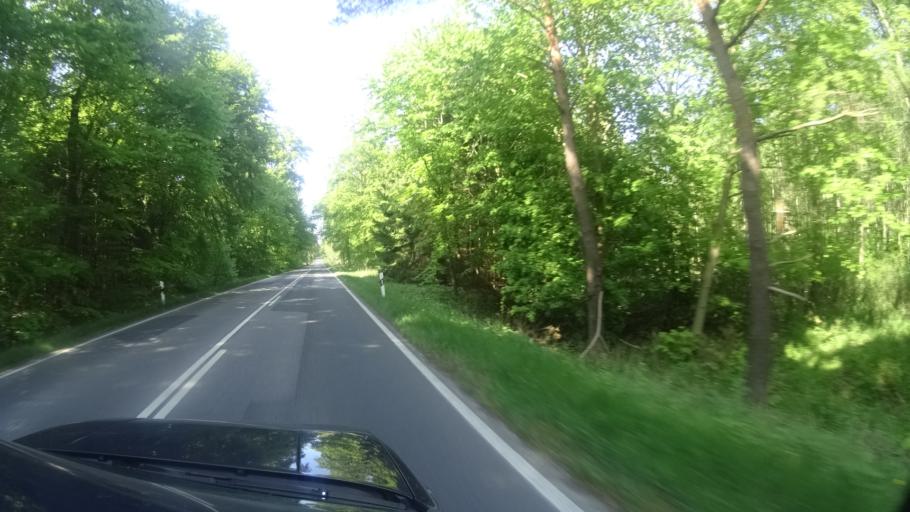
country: DE
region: Mecklenburg-Vorpommern
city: Rovershagen
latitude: 54.1943
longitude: 12.2113
